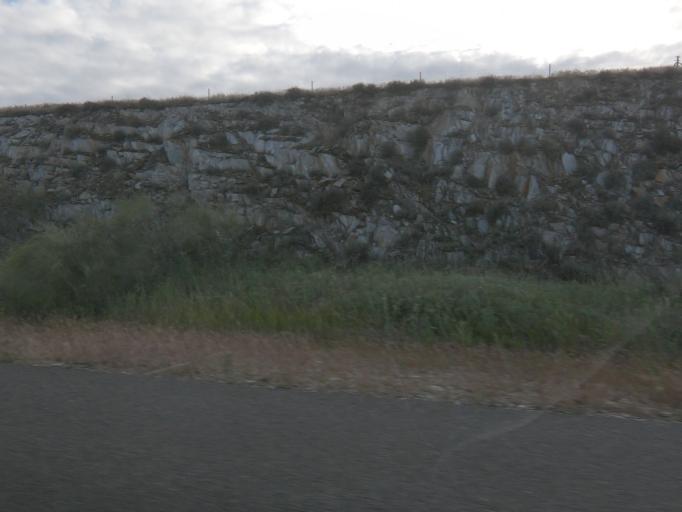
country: ES
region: Extremadura
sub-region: Provincia de Caceres
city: Casar de Caceres
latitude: 39.5630
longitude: -6.4003
